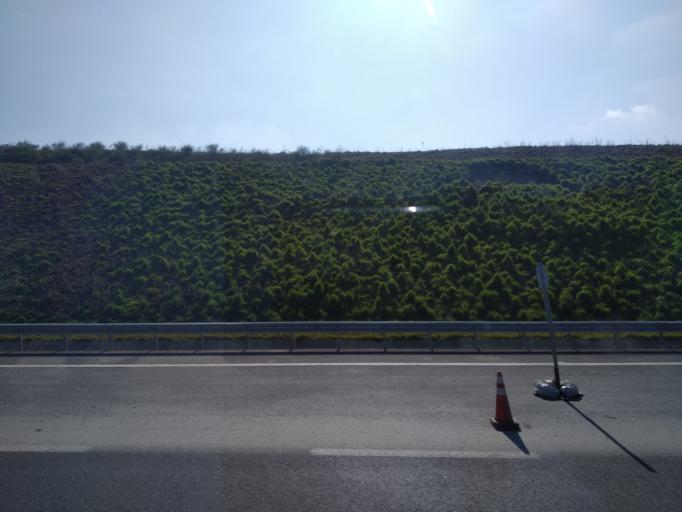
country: TR
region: Istanbul
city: Kemerburgaz
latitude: 41.2294
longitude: 28.8569
